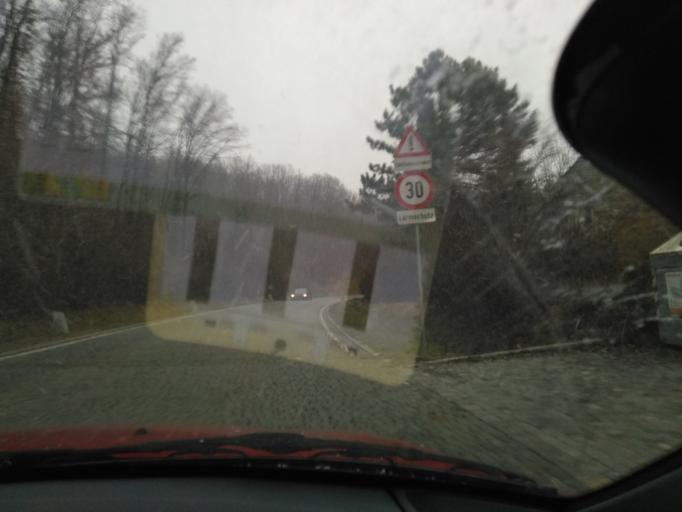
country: AT
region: Lower Austria
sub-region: Politischer Bezirk Wien-Umgebung
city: Klosterneuburg
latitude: 48.2534
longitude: 16.2738
